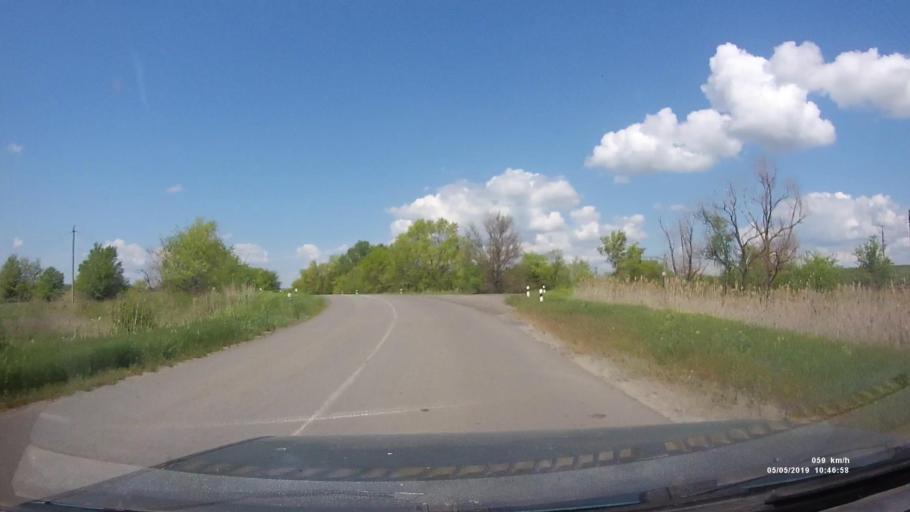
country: RU
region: Rostov
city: Ust'-Donetskiy
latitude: 47.6371
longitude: 40.8386
